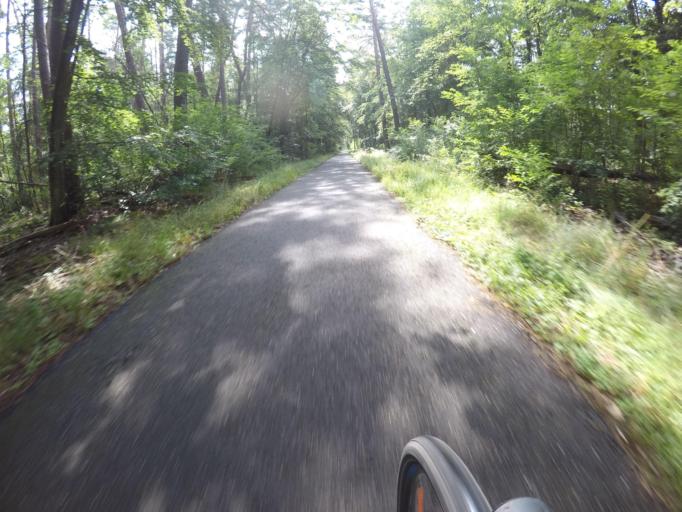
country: DE
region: Baden-Wuerttemberg
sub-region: Karlsruhe Region
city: Reilingen
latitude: 49.3193
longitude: 8.5994
